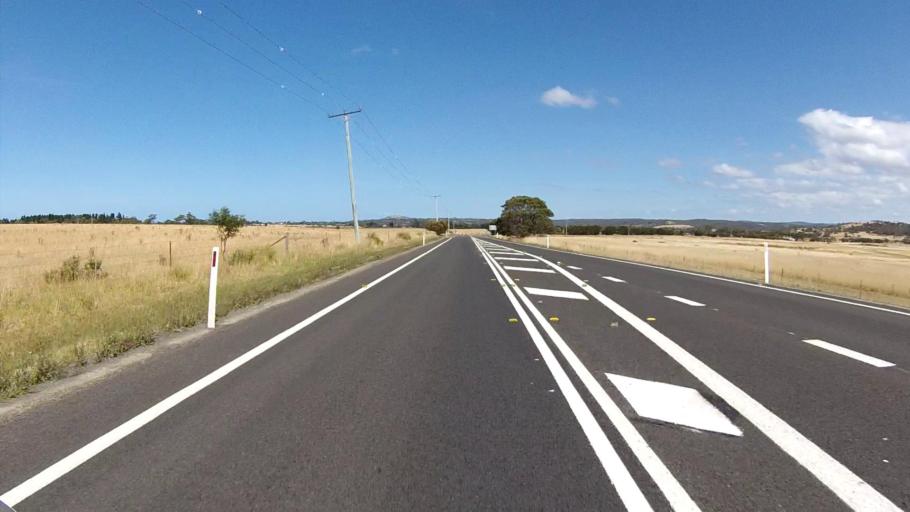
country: AU
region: Tasmania
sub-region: Break O'Day
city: St Helens
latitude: -42.0988
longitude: 148.0630
